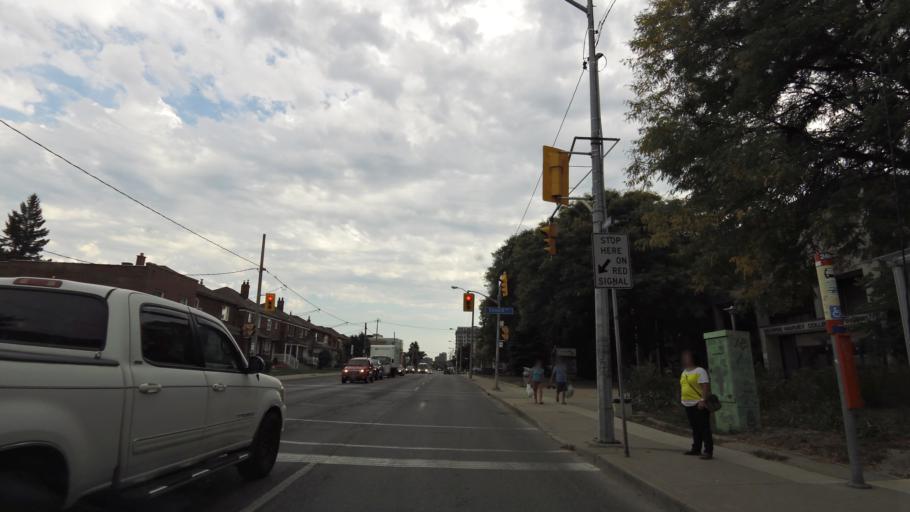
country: CA
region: Ontario
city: Toronto
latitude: 43.6849
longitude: -79.4729
